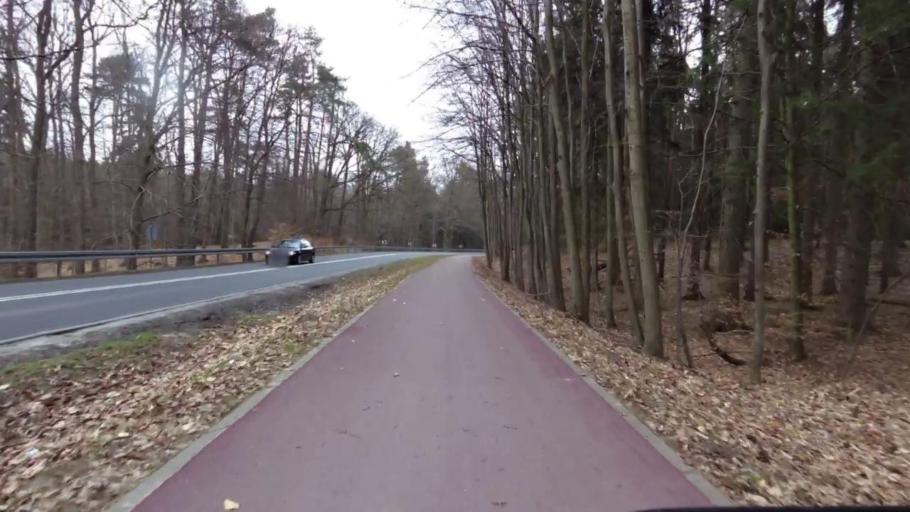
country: PL
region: West Pomeranian Voivodeship
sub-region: Powiat koszalinski
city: Sianow
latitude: 54.2086
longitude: 16.2374
